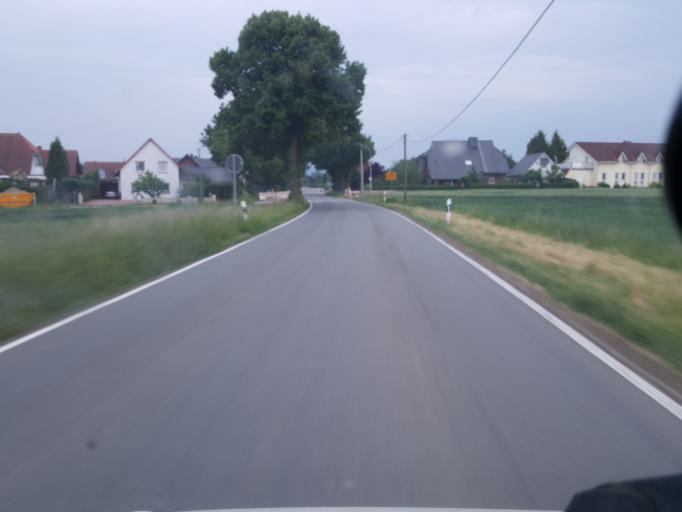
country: DE
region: North Rhine-Westphalia
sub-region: Regierungsbezirk Detmold
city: Hille
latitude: 52.3224
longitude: 8.8313
